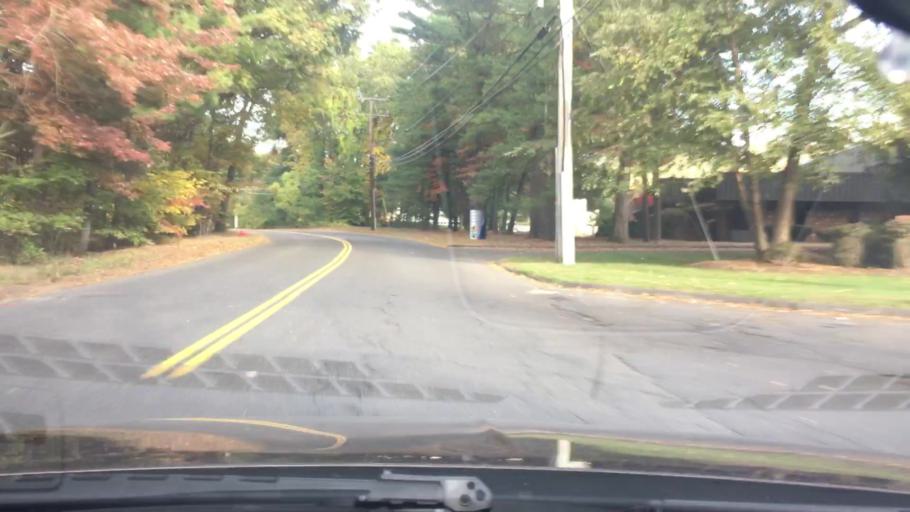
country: US
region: Connecticut
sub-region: Hartford County
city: Plainville
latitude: 41.7015
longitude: -72.8564
